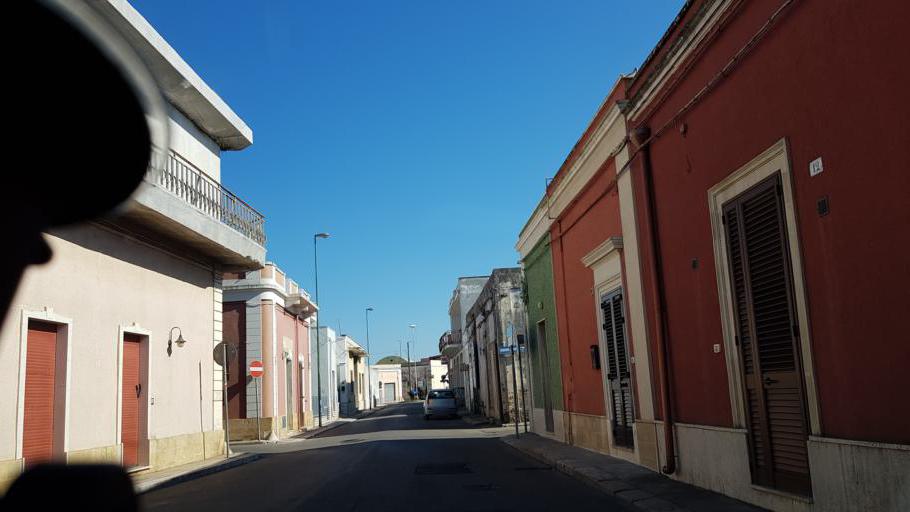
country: IT
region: Apulia
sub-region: Provincia di Brindisi
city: Torchiarolo
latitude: 40.4863
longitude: 18.0511
